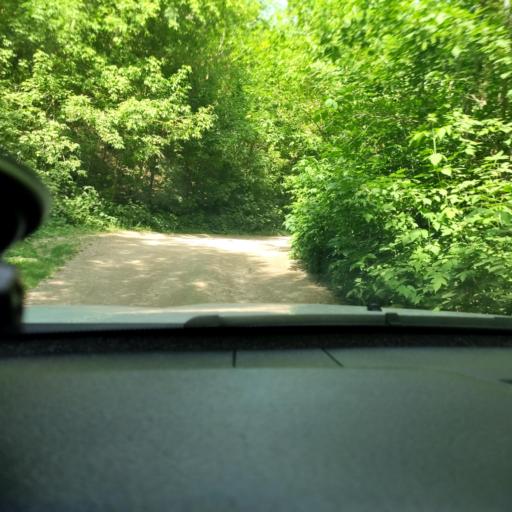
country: RU
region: Samara
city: Volzhskiy
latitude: 53.3369
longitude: 50.2012
